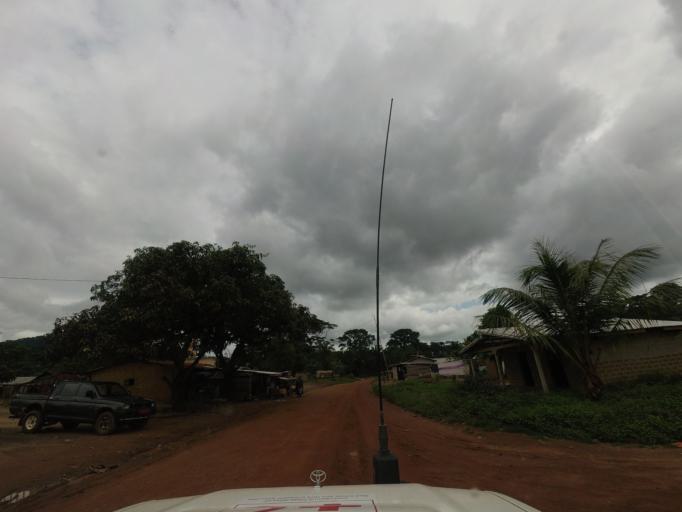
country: LR
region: Nimba
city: Sanniquellie
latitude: 7.3196
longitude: -8.9668
